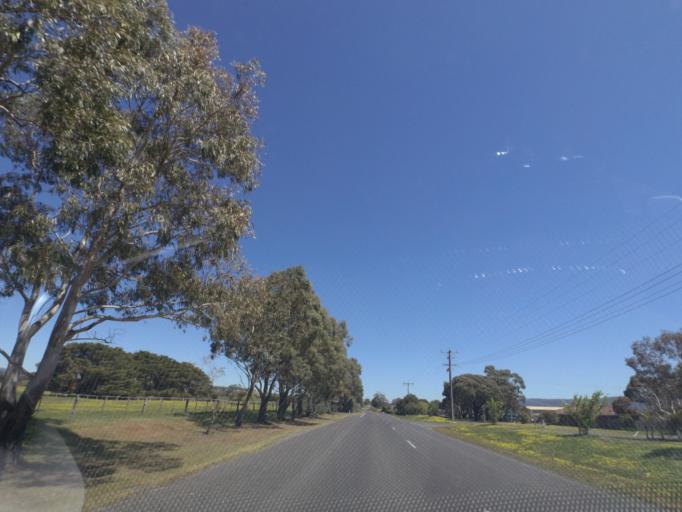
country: AU
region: Victoria
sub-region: Hume
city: Sunbury
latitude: -37.2792
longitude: 144.7179
